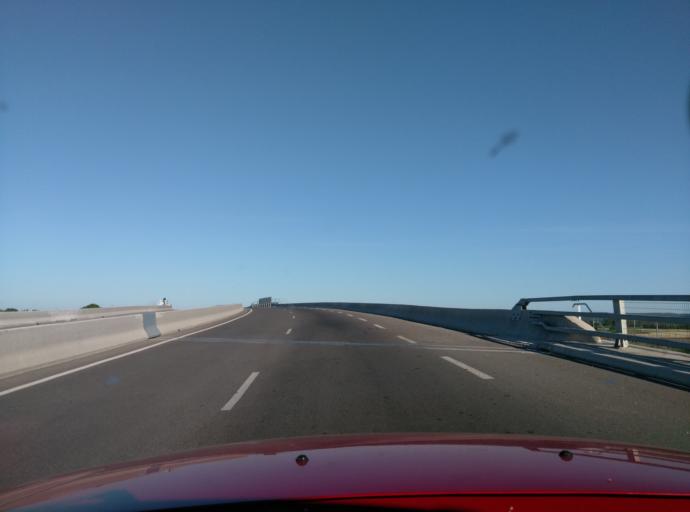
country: FR
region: Languedoc-Roussillon
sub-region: Departement du Gard
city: Manduel
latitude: 43.8300
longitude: 4.4764
